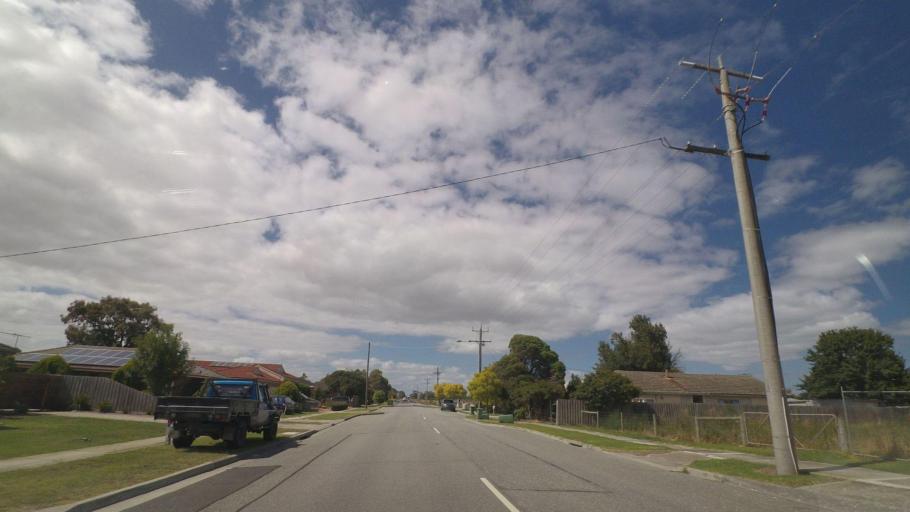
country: AU
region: Victoria
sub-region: Cardinia
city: Koo-Wee-Rup
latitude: -38.2038
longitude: 145.4902
